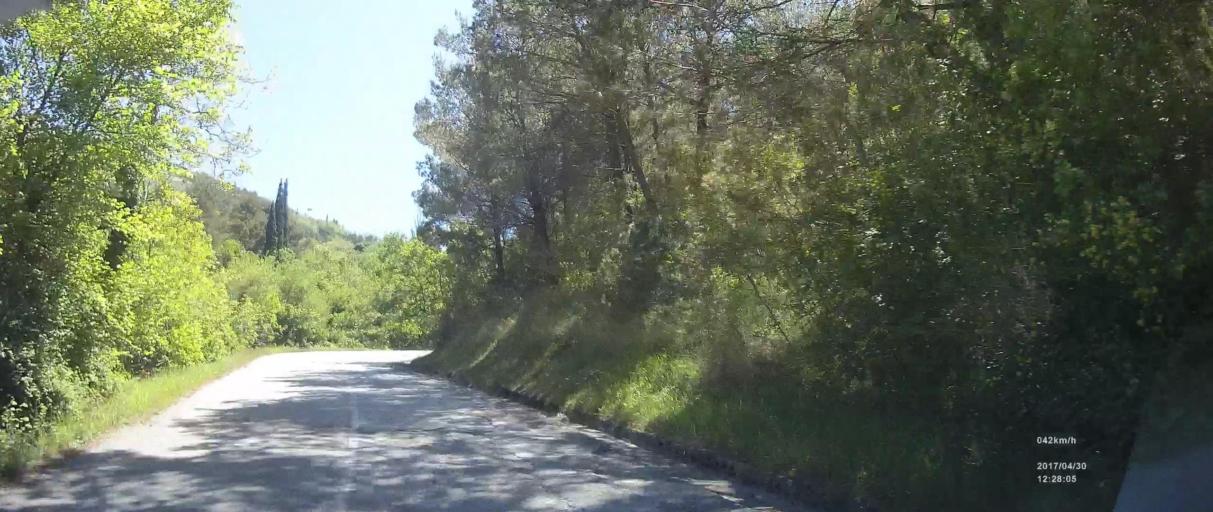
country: HR
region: Splitsko-Dalmatinska
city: Srinjine
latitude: 43.5039
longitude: 16.5993
